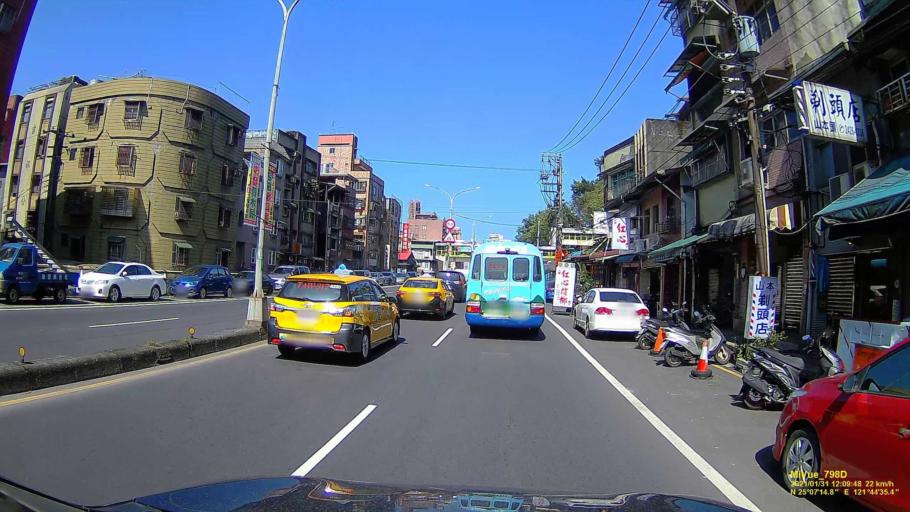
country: TW
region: Taiwan
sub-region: Keelung
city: Keelung
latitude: 25.1210
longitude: 121.7431
